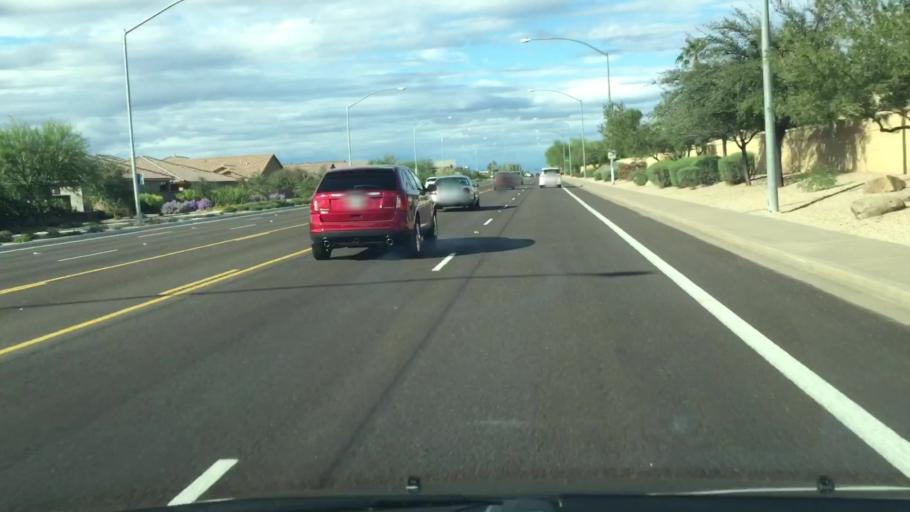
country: US
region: Arizona
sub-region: Maricopa County
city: Mesa
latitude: 33.4413
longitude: -111.7189
